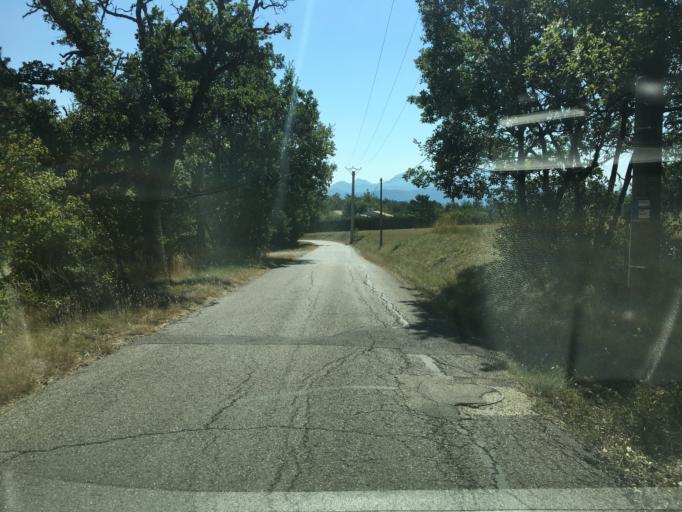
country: FR
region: Provence-Alpes-Cote d'Azur
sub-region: Departement des Alpes-de-Haute-Provence
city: Mallemoisson
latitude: 44.0686
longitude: 6.1360
